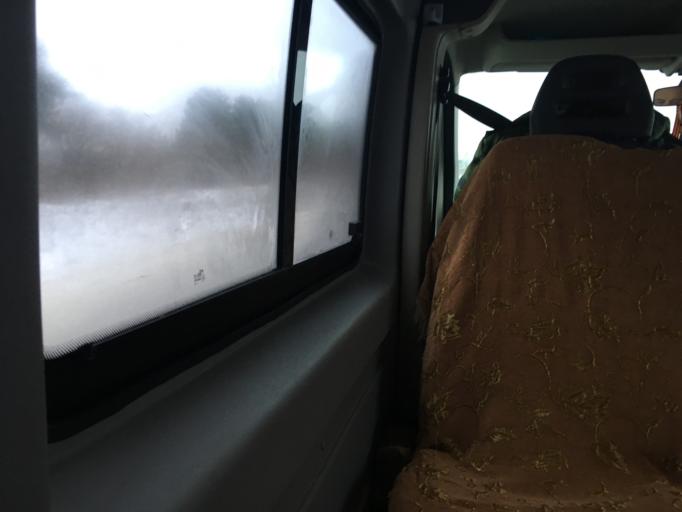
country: RU
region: Tula
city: Dubna
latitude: 54.0586
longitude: 37.0314
